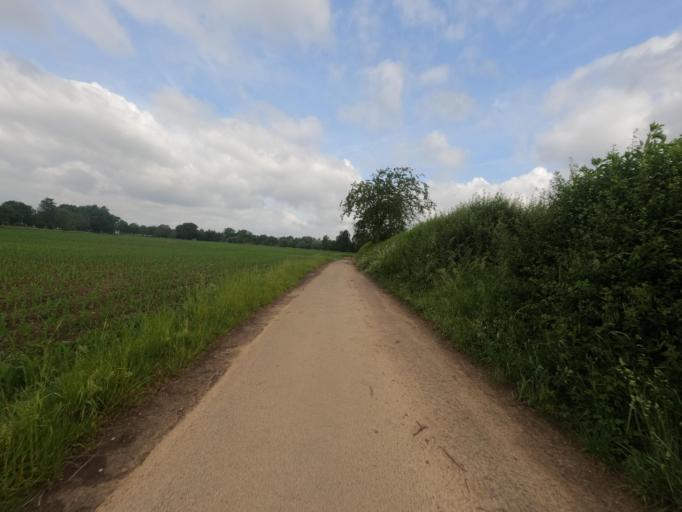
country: DE
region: North Rhine-Westphalia
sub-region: Regierungsbezirk Koln
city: Heinsberg
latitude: 51.0958
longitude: 6.1123
